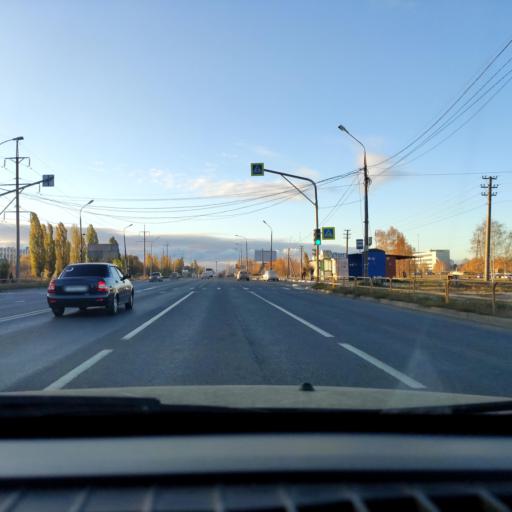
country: RU
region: Samara
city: Tol'yatti
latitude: 53.5647
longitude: 49.2901
